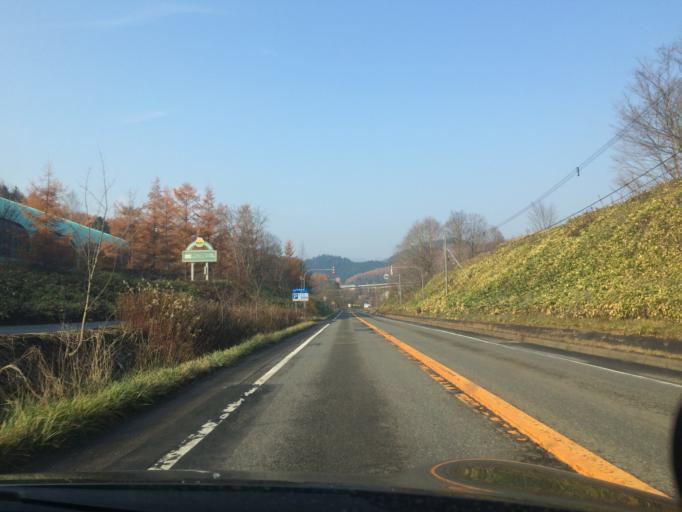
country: JP
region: Hokkaido
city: Iwamizawa
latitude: 42.9324
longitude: 142.0893
